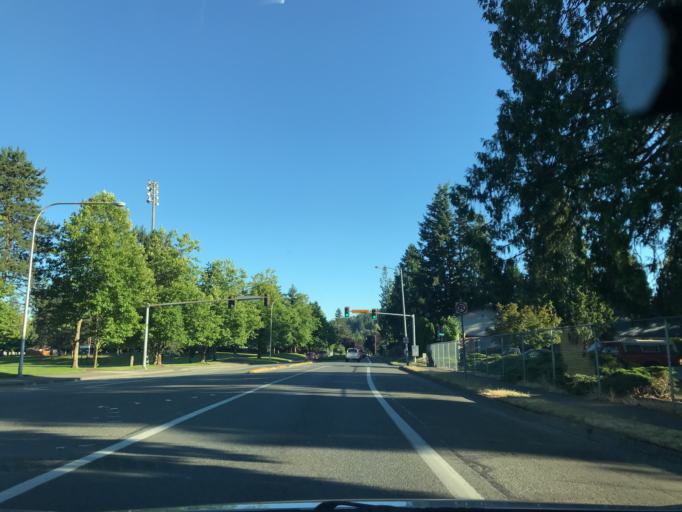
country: US
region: Washington
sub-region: King County
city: Auburn
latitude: 47.2813
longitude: -122.2080
